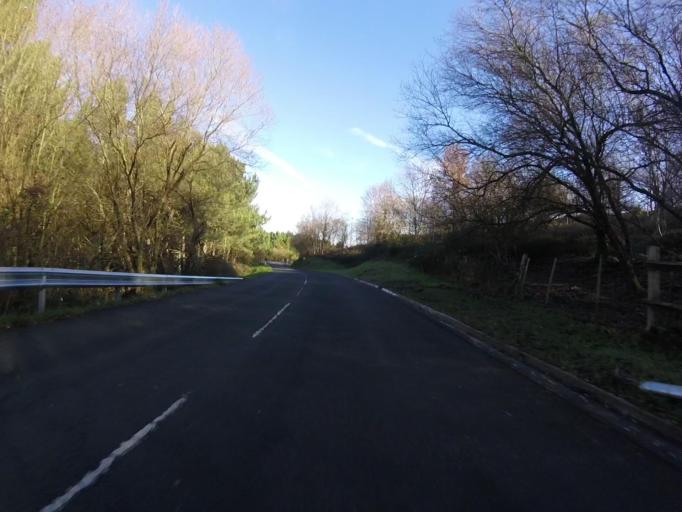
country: ES
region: Basque Country
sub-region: Provincia de Guipuzcoa
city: Fuenterrabia
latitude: 43.3642
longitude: -1.8314
